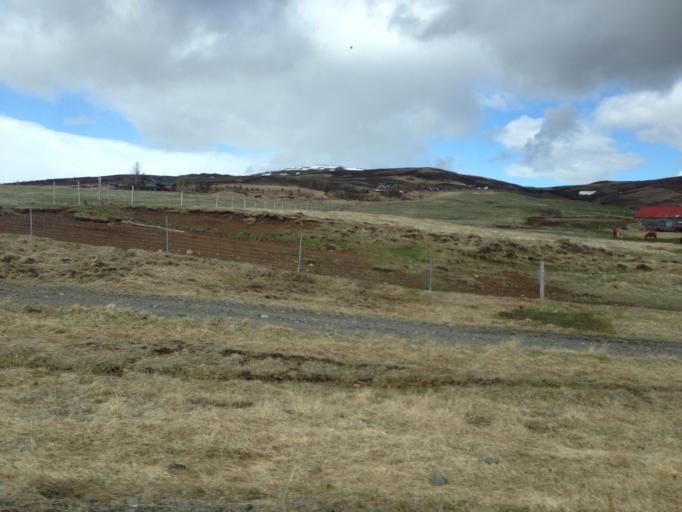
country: IS
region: South
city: Selfoss
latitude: 64.2744
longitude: -20.4048
